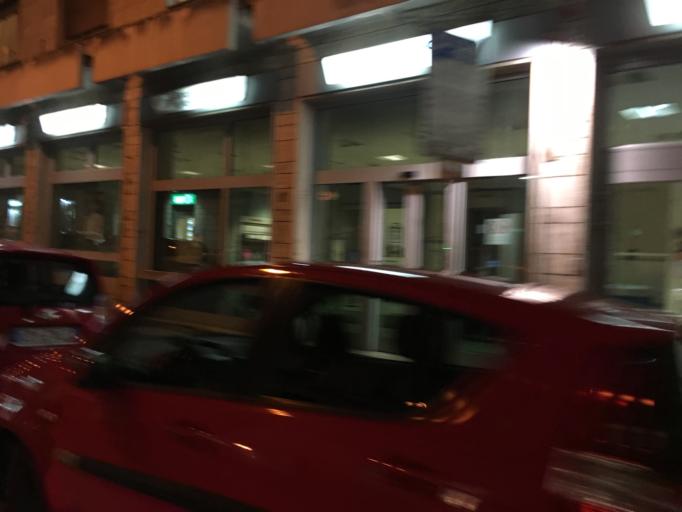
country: IT
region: Campania
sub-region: Provincia di Napoli
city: Napoli
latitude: 40.8316
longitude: 14.2223
